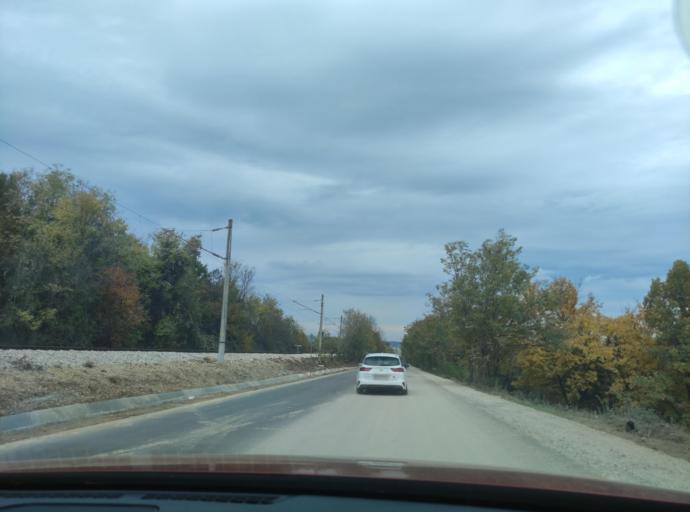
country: BG
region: Montana
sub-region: Obshtina Montana
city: Montana
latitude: 43.3862
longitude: 23.2433
